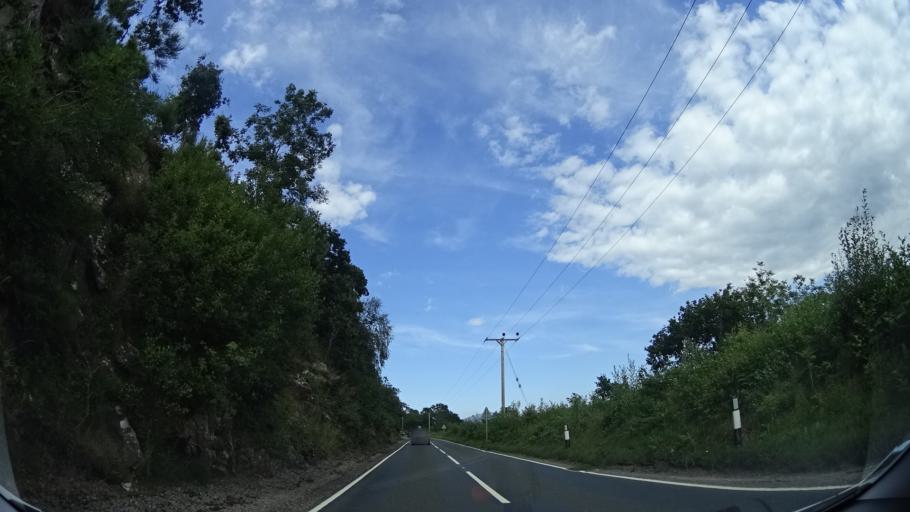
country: GB
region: Scotland
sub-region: Highland
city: Beauly
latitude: 57.2536
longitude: -4.5307
